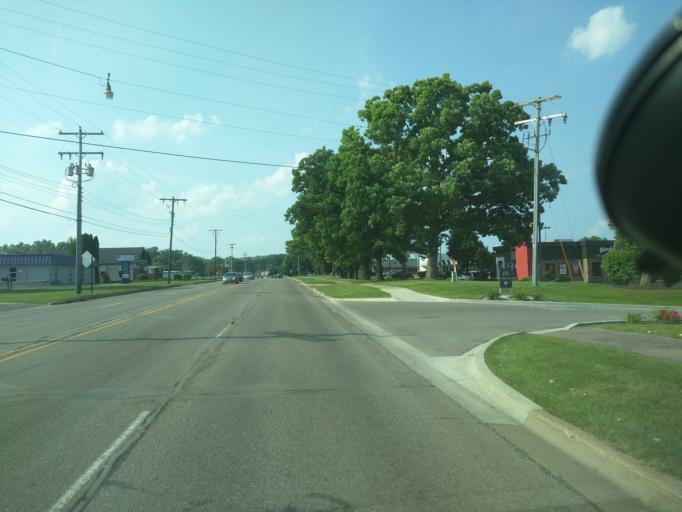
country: US
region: Michigan
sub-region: Jackson County
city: Jackson
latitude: 42.2725
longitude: -84.4529
